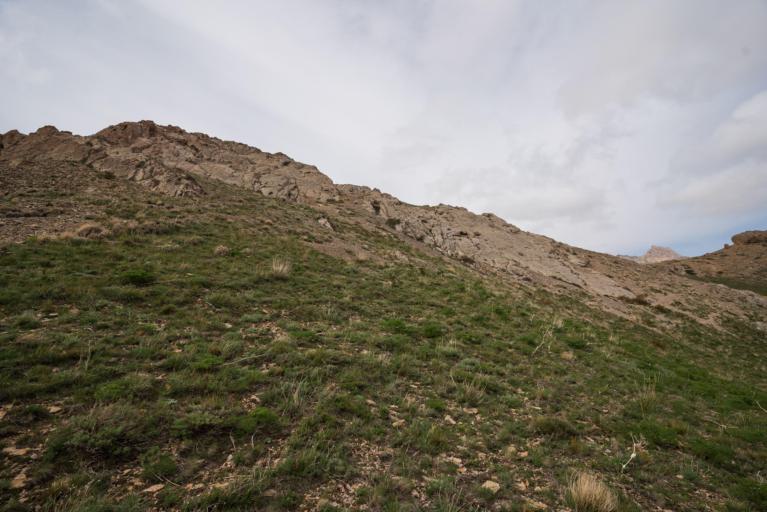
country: KZ
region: Ongtustik Qazaqstan
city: Ashchysay
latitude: 43.7480
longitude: 68.8274
